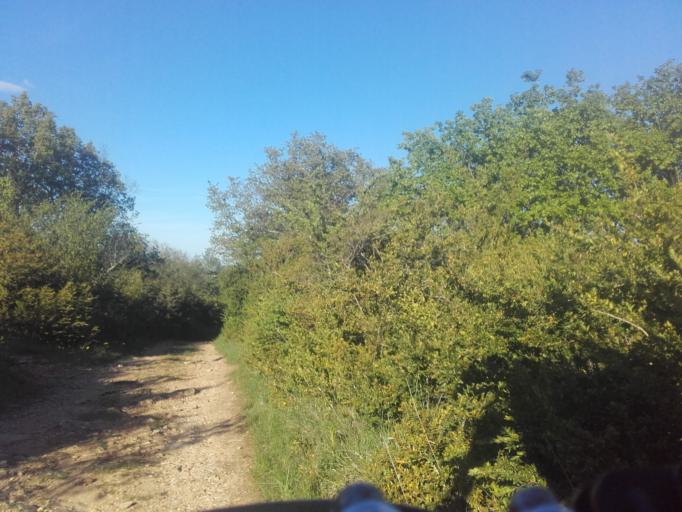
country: FR
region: Bourgogne
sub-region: Departement de Saone-et-Loire
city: Rully
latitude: 46.8827
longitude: 4.7345
